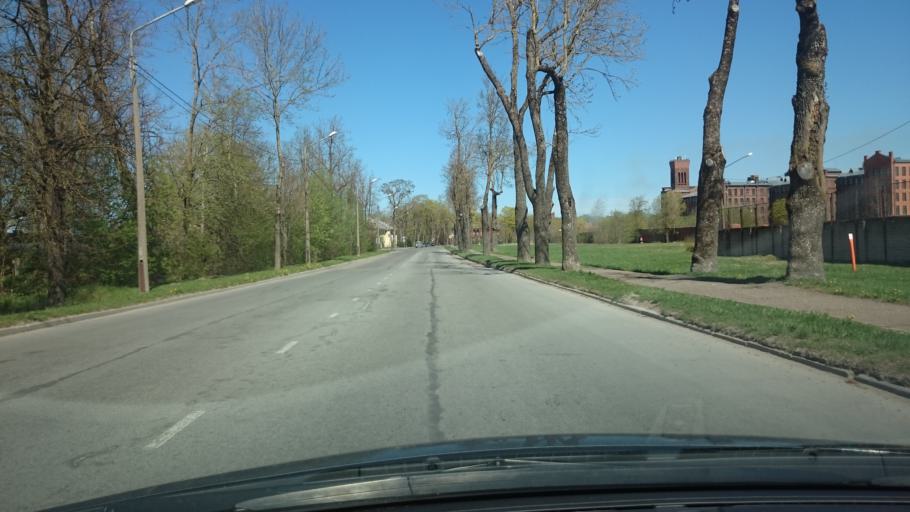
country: EE
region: Ida-Virumaa
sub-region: Narva linn
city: Narva
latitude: 59.3573
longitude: 28.1850
